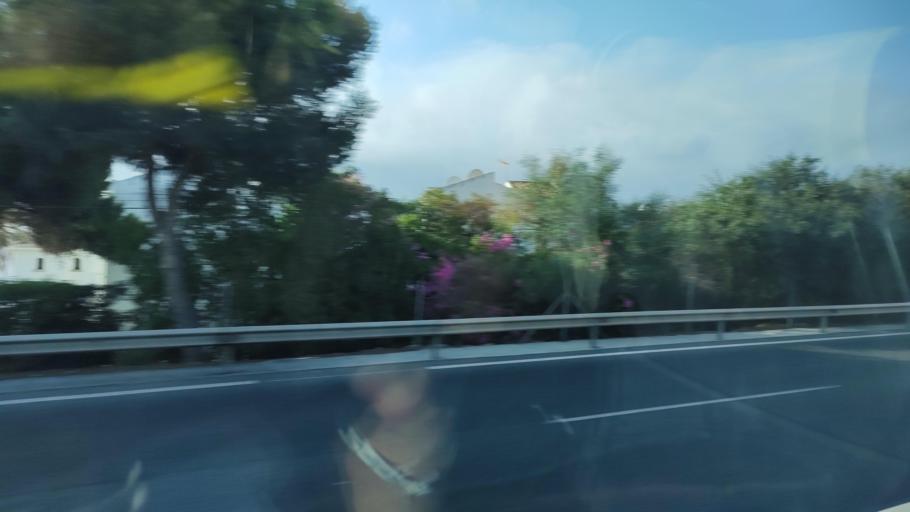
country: ES
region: Andalusia
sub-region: Provincia de Malaga
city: Fuengirola
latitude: 36.4924
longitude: -4.6926
